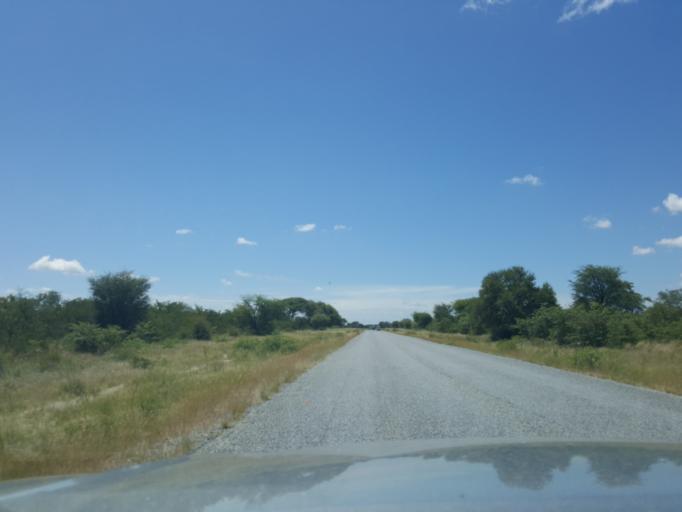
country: BW
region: Central
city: Nata
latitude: -20.1507
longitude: 25.7694
